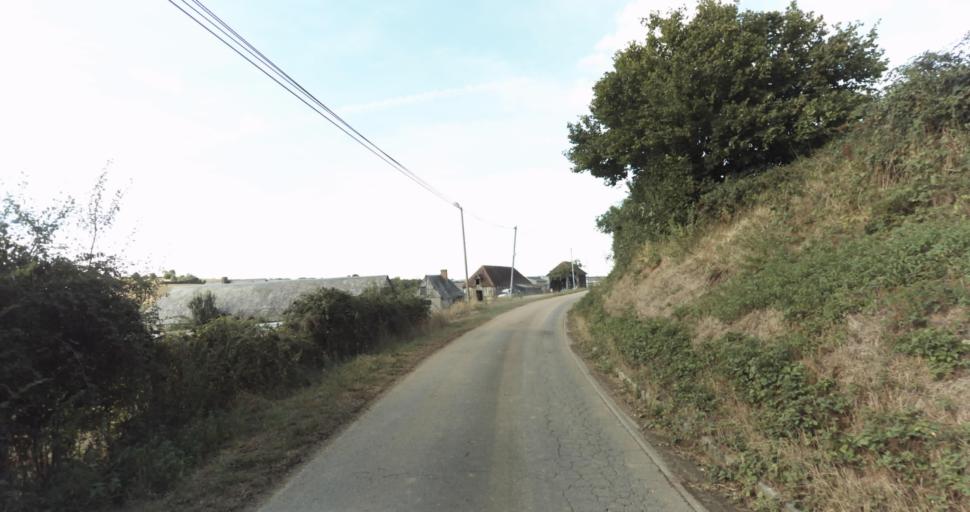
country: FR
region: Lower Normandy
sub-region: Departement de l'Orne
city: Vimoutiers
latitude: 48.9300
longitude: 0.1309
